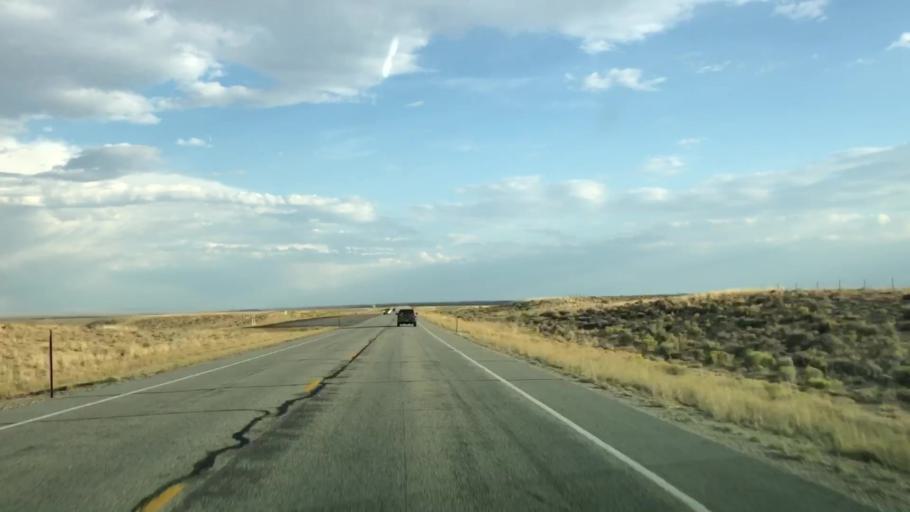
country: US
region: Wyoming
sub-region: Sublette County
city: Marbleton
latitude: 42.3290
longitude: -109.5147
